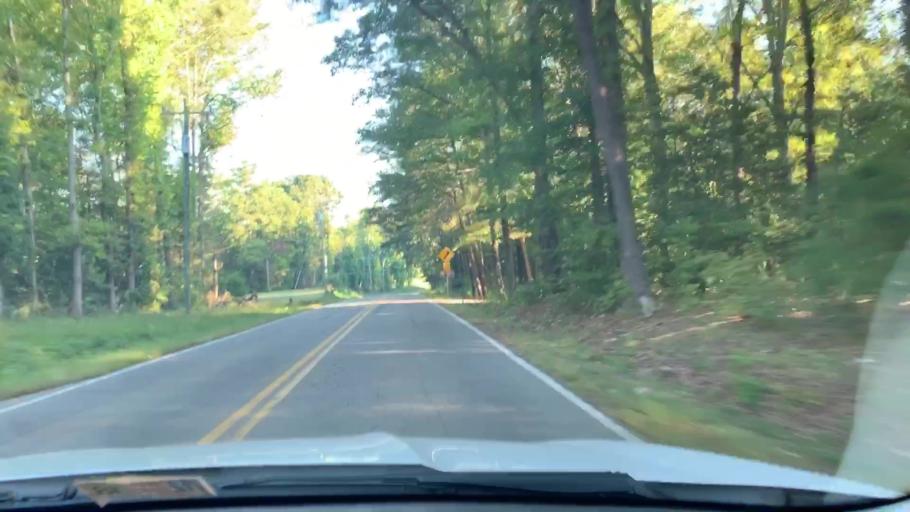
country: US
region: Virginia
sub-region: Middlesex County
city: Deltaville
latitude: 37.5576
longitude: -76.4513
